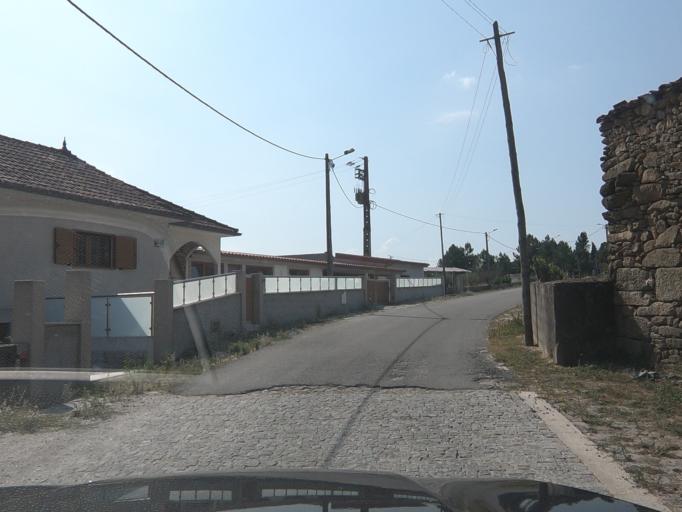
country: PT
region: Vila Real
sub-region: Sabrosa
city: Sabrosa
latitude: 41.3334
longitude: -7.6065
